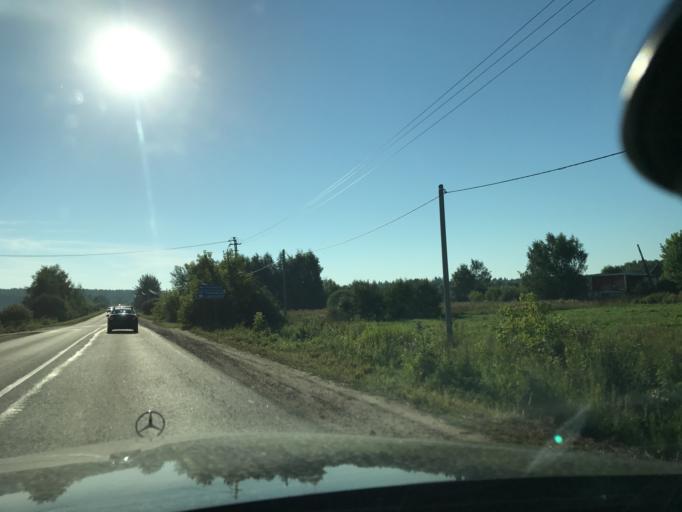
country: RU
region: Moskovskaya
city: Bakhchivandzhi
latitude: 55.8612
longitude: 38.0464
